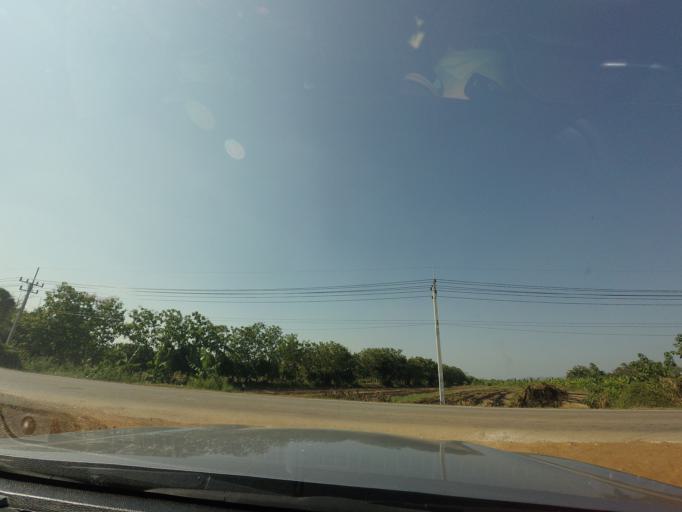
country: TH
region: Sukhothai
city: Sawankhalok
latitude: 17.3250
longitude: 99.8202
